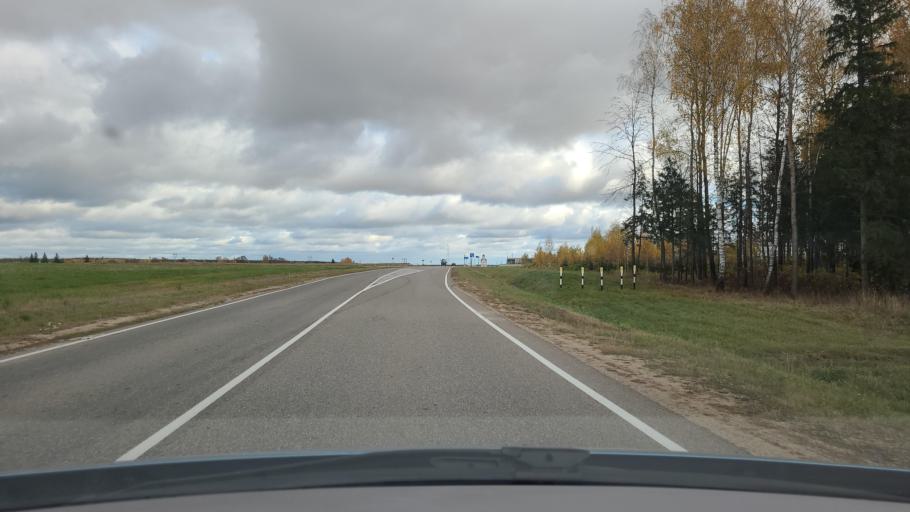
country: BY
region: Grodnenskaya
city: Astravyets
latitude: 54.7671
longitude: 26.0789
